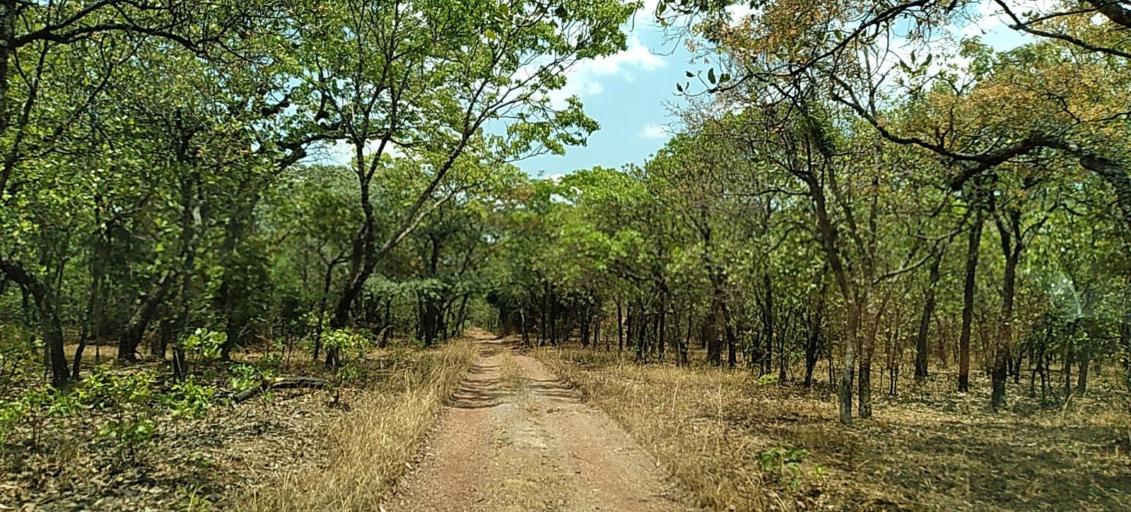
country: ZM
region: Copperbelt
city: Chililabombwe
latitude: -12.4589
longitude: 27.6985
